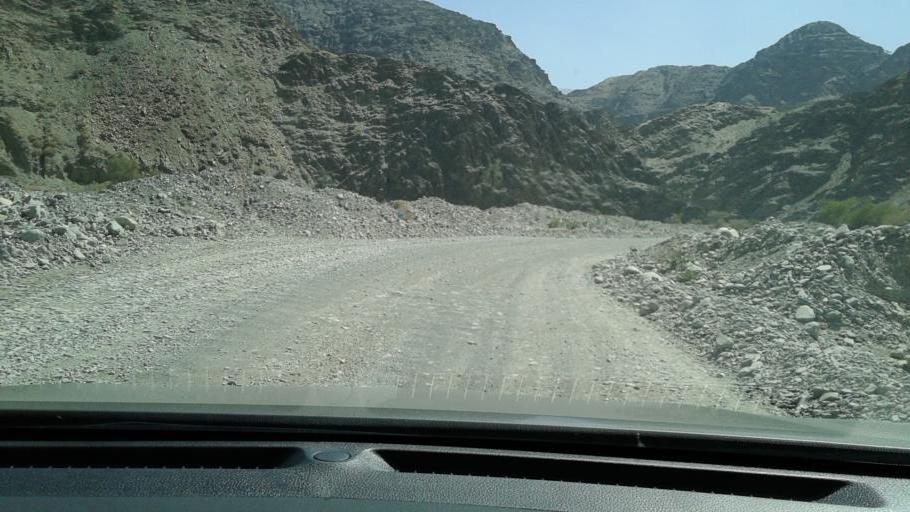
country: OM
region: Al Batinah
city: Bayt al `Awabi
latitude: 23.2595
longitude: 57.4421
